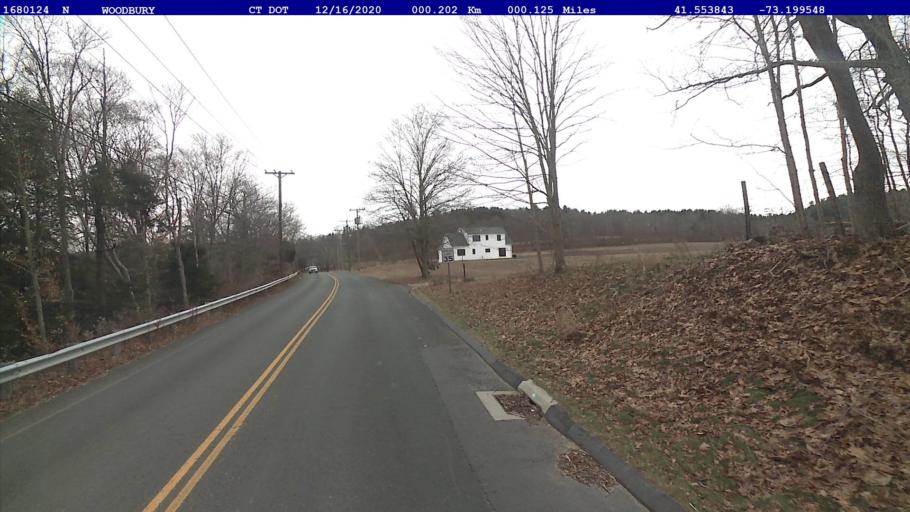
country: US
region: Connecticut
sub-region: Litchfield County
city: Woodbury Center
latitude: 41.5539
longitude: -73.1994
